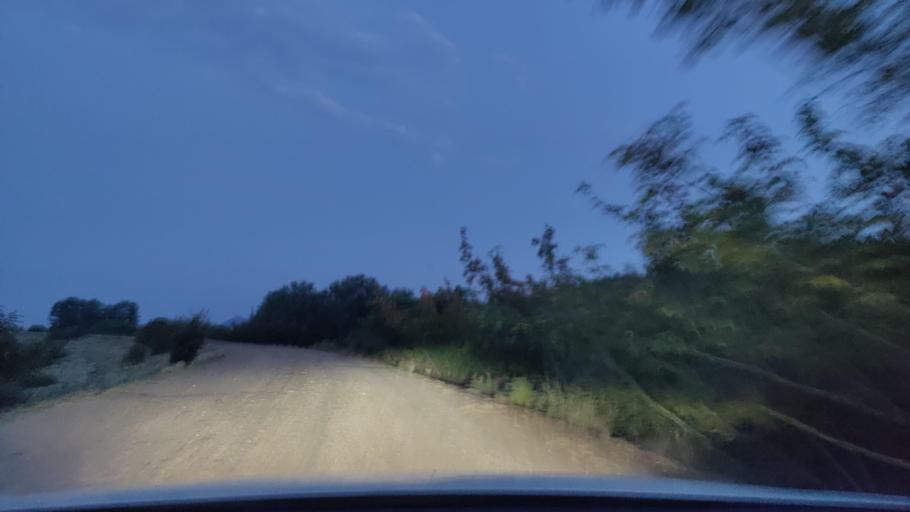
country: GR
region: Central Macedonia
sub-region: Nomos Serron
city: Chrysochorafa
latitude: 41.2009
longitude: 23.0826
